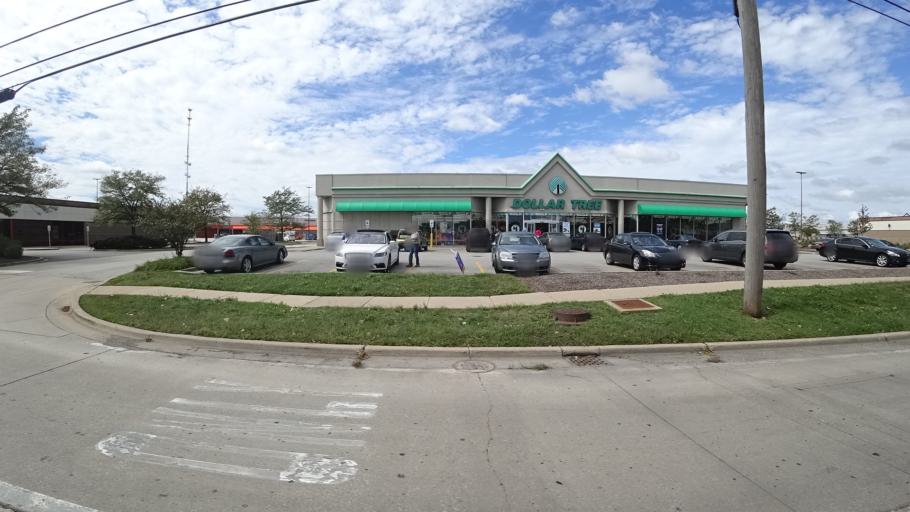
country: US
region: Illinois
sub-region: Cook County
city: Chicago Ridge
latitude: 41.7105
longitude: -87.7797
